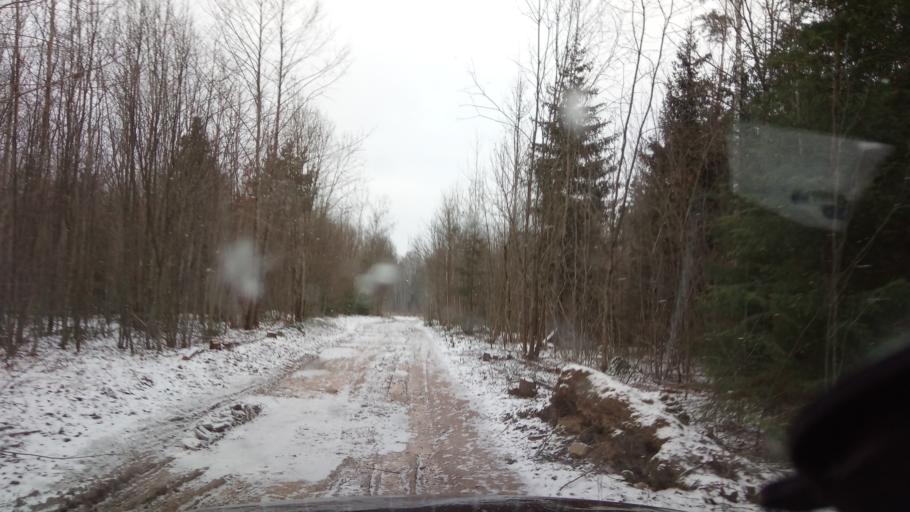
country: LT
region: Alytaus apskritis
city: Varena
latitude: 54.1360
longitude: 24.6999
